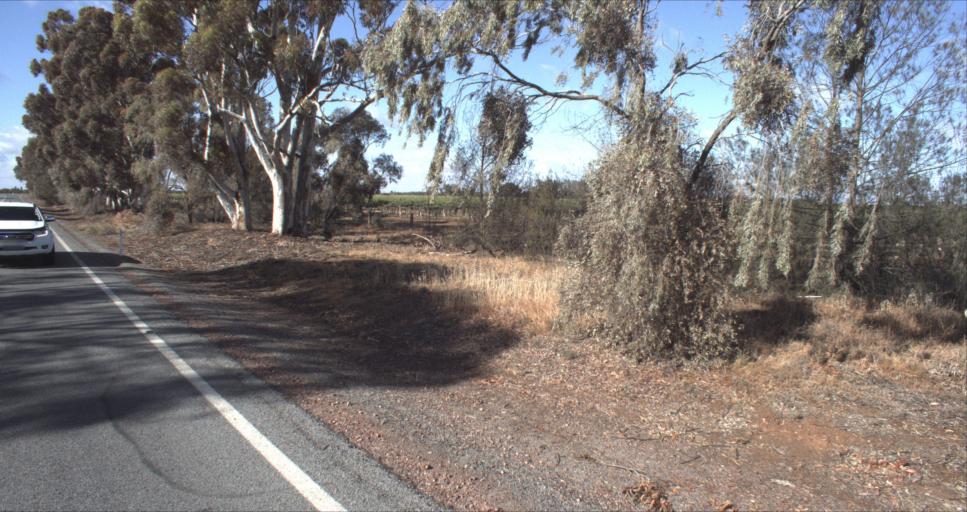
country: AU
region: New South Wales
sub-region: Leeton
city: Leeton
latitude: -34.5467
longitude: 146.3545
